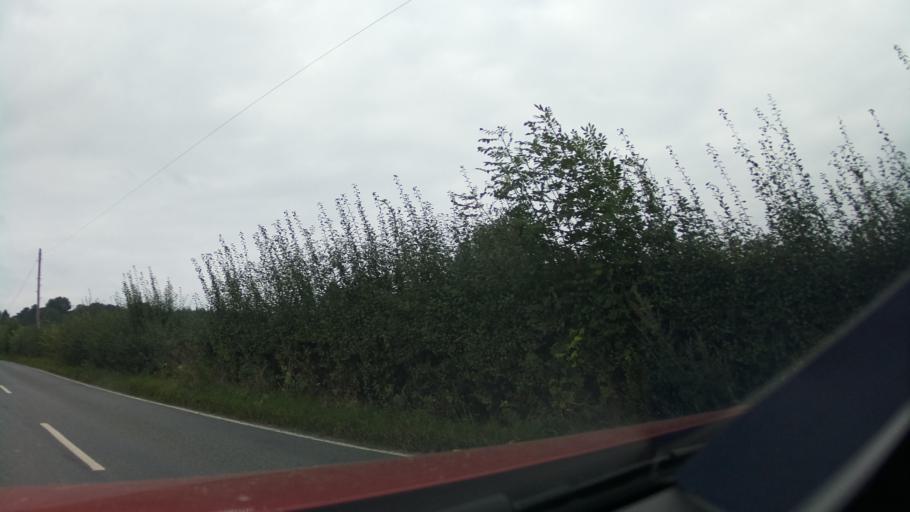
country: GB
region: England
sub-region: Derbyshire
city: Wirksworth
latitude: 53.0175
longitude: -1.5912
